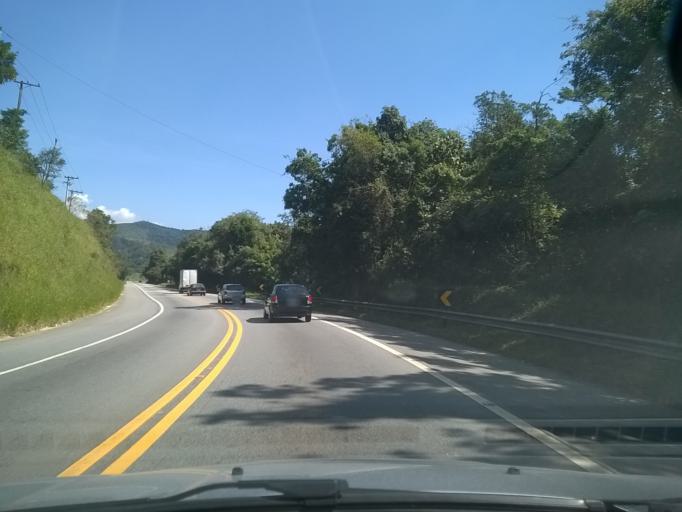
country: BR
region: Sao Paulo
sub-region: Francisco Morato
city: Francisco Morato
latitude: -23.2867
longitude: -46.7905
